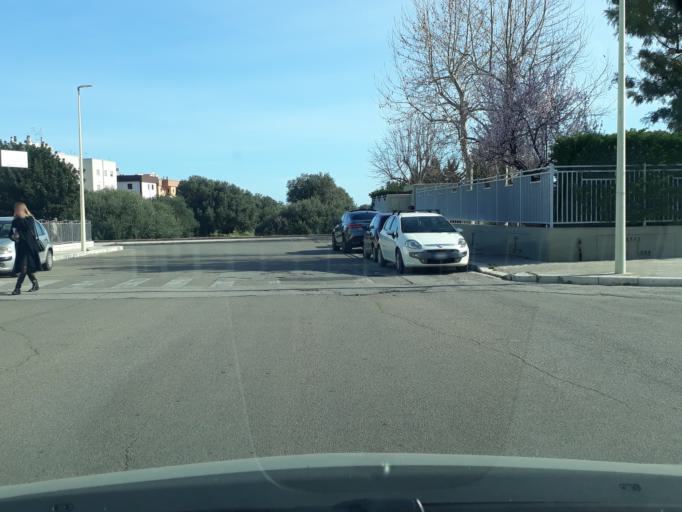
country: IT
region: Apulia
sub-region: Provincia di Brindisi
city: Fasano
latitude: 40.8290
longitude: 17.3627
